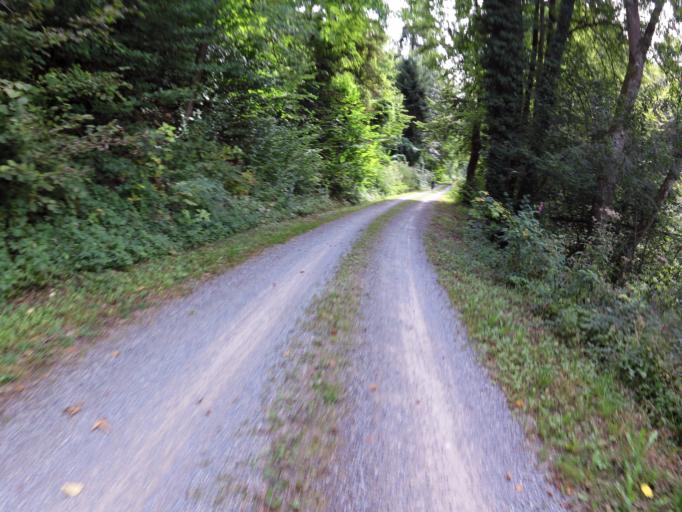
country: DE
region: Baden-Wuerttemberg
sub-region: Freiburg Region
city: Sulz am Neckar
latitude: 48.3451
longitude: 8.5951
